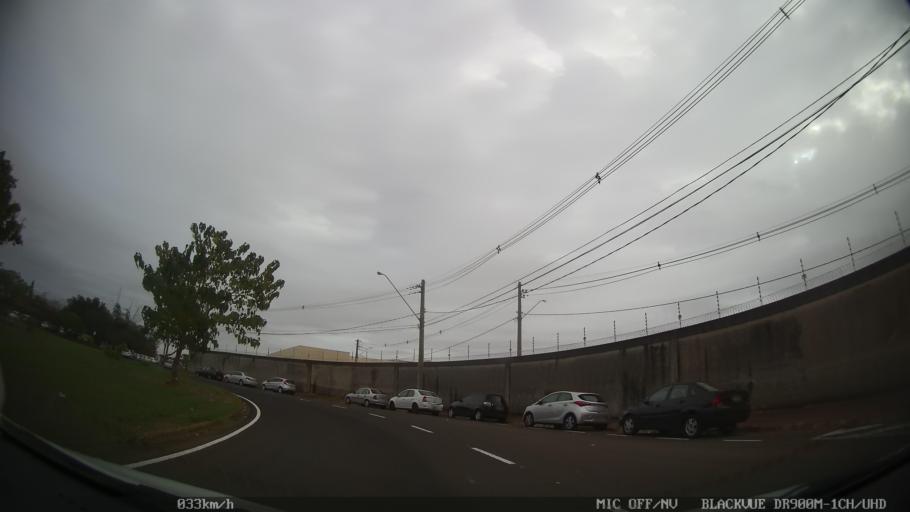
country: BR
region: Sao Paulo
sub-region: Sao Jose Do Rio Preto
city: Sao Jose do Rio Preto
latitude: -20.8277
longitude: -49.4190
